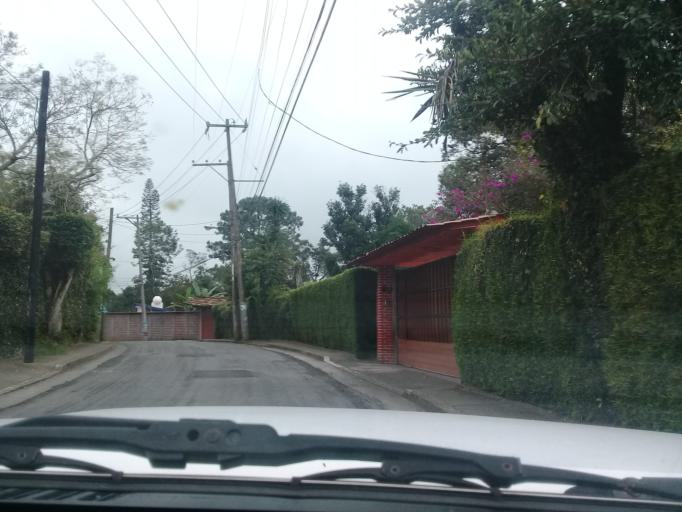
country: MX
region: Veracruz
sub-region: Xalapa
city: Xalapa de Enriquez
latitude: 19.5123
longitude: -96.9102
